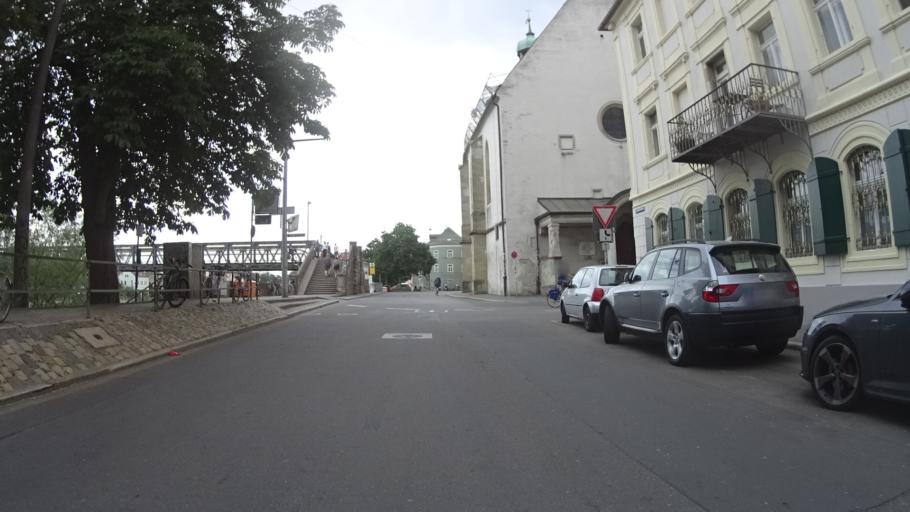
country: DE
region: Bavaria
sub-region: Upper Palatinate
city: Lappersdorf
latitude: 49.0218
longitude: 12.0903
